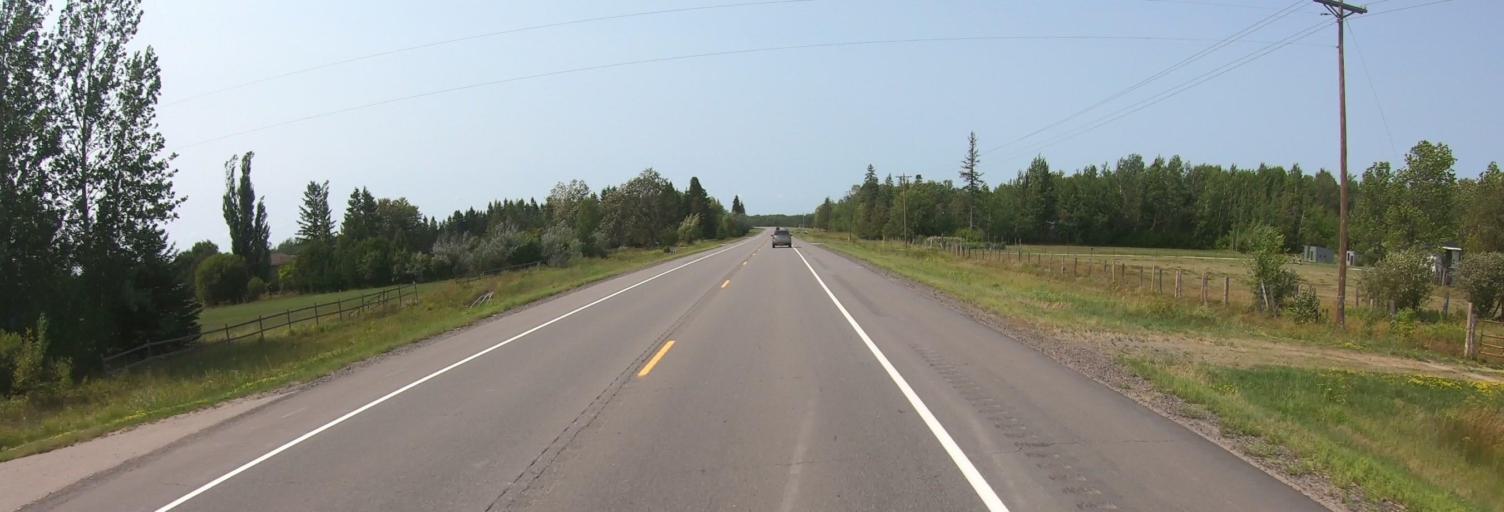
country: US
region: Minnesota
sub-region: Koochiching County
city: International Falls
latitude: 48.5344
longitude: -93.4966
